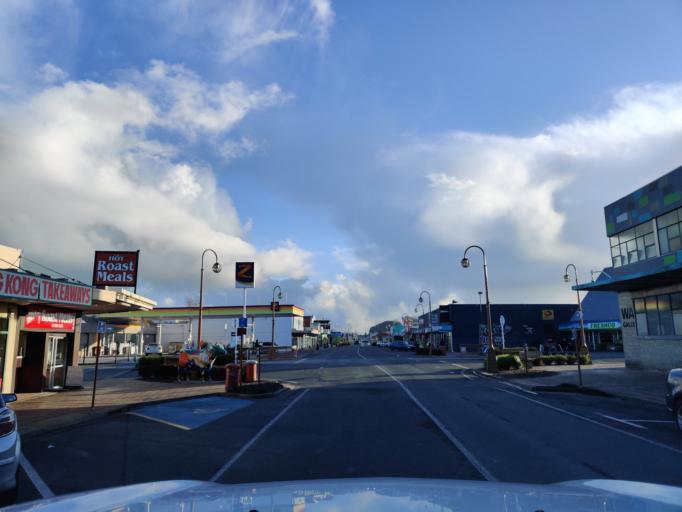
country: NZ
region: Waikato
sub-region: Waipa District
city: Cambridge
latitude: -37.6585
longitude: 175.5272
